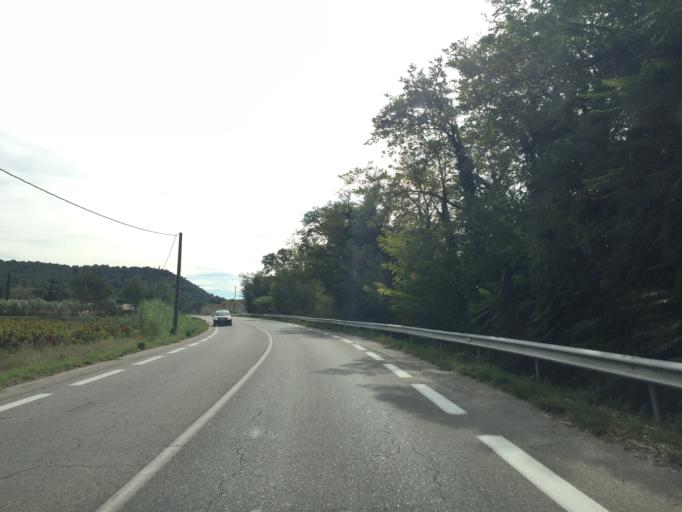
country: FR
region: Provence-Alpes-Cote d'Azur
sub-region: Departement du Vaucluse
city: Mondragon
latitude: 44.2520
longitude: 4.7318
